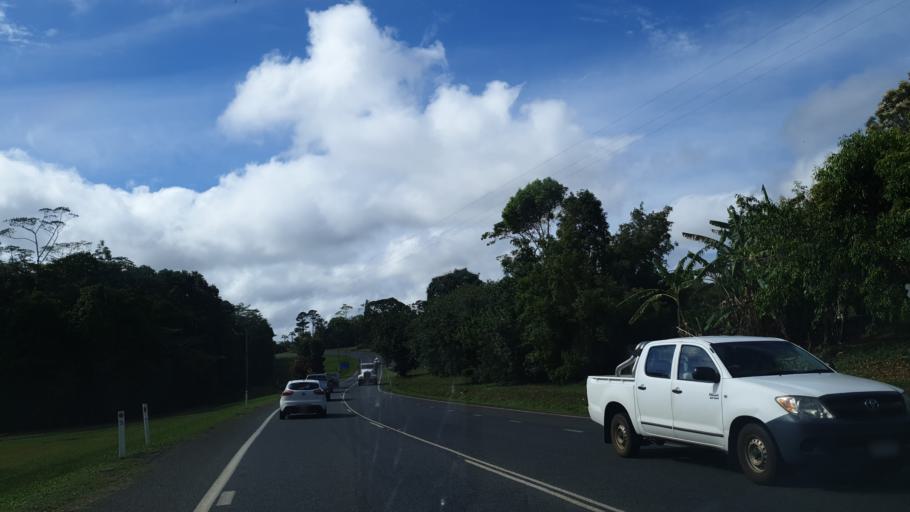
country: AU
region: Queensland
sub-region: Tablelands
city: Atherton
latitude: -17.3520
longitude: 145.5828
